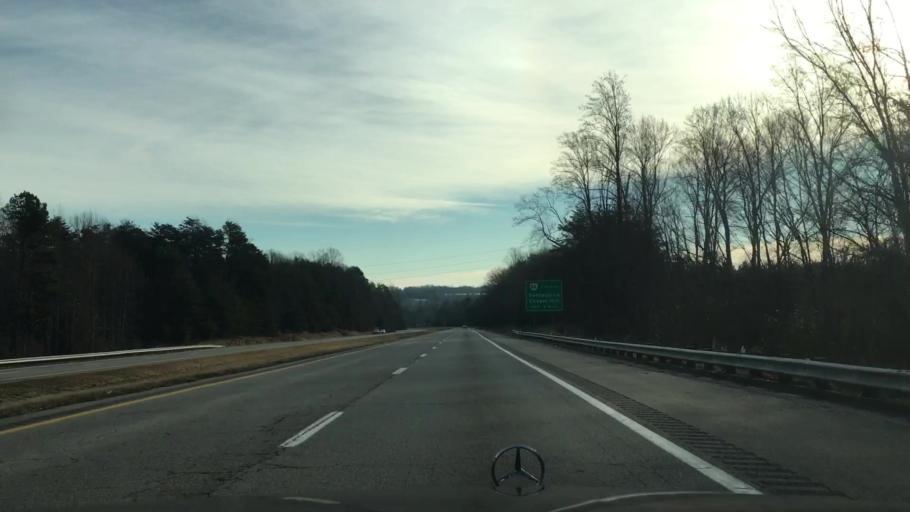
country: US
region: Virginia
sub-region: City of Danville
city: Danville
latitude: 36.5457
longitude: -79.4242
